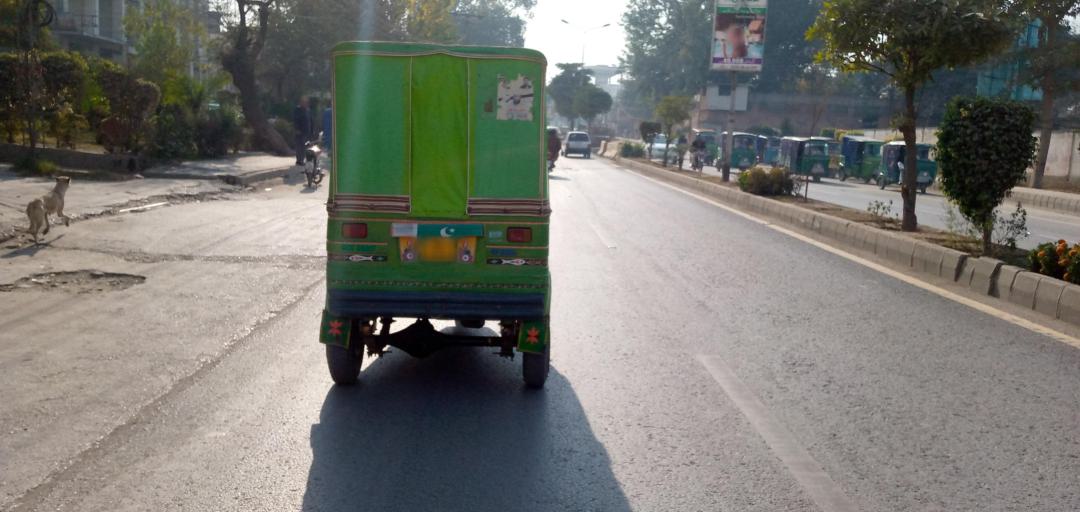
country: PK
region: Khyber Pakhtunkhwa
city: Peshawar
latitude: 33.9913
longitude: 71.5330
